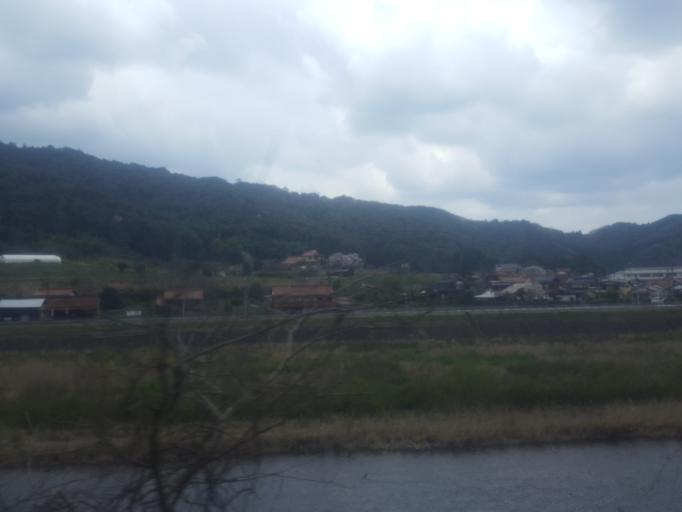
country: JP
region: Shimane
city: Masuda
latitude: 34.5750
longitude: 131.7976
